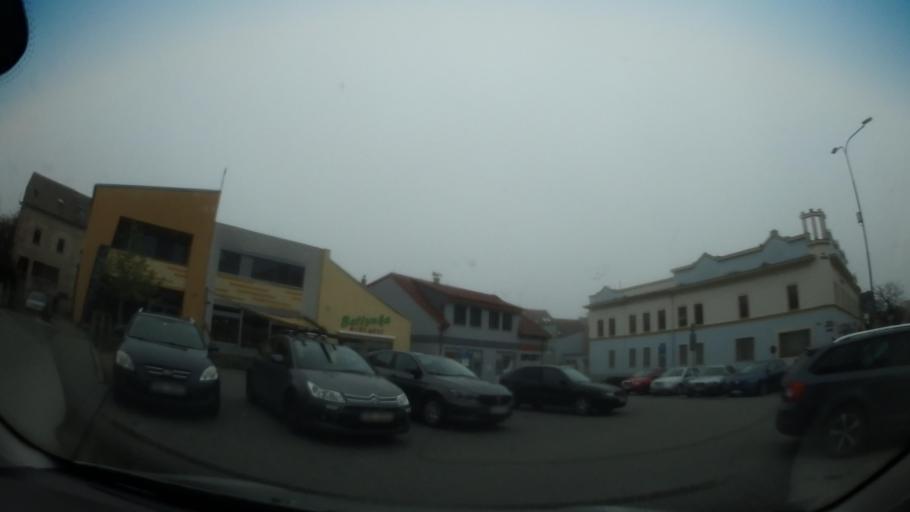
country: CZ
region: South Moravian
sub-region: Okres Hodonin
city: Kyjov
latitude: 49.0112
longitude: 17.1261
